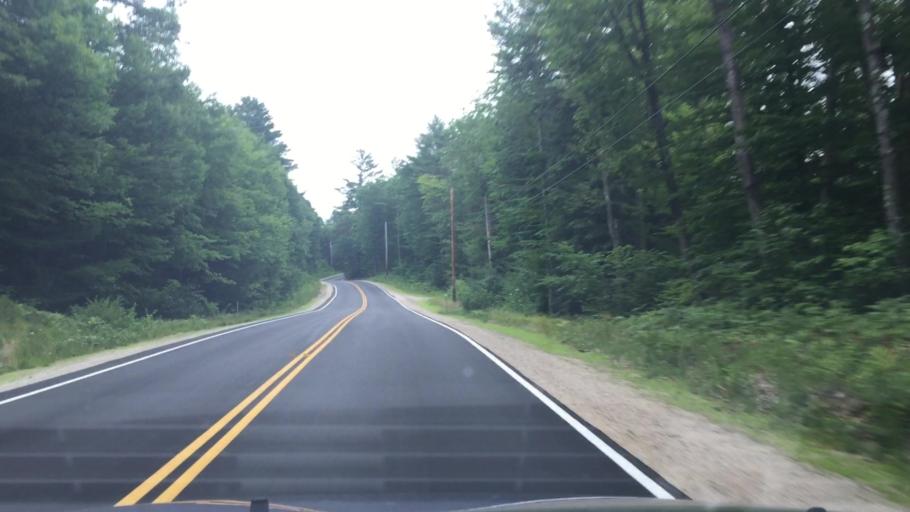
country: US
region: New Hampshire
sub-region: Carroll County
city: Freedom
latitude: 43.8444
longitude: -71.0882
